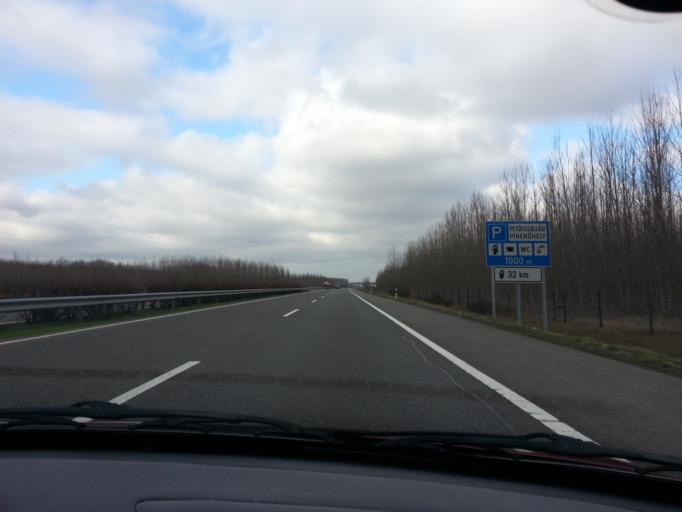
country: HU
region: Csongrad
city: Csengele
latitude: 46.5959
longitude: 19.8512
